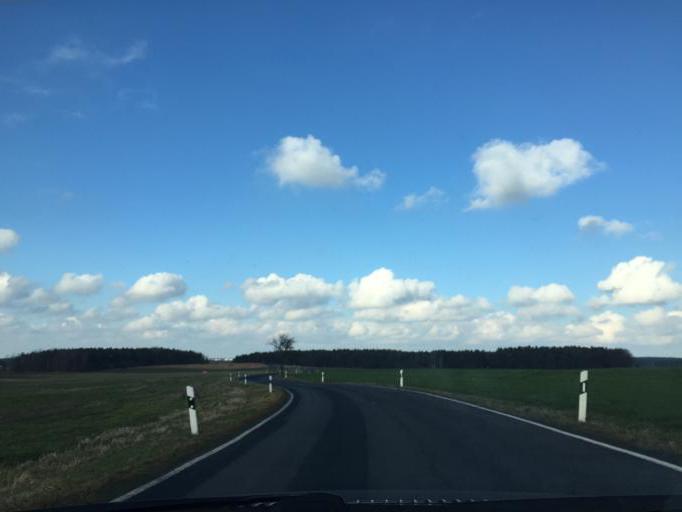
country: DE
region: Saxony
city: Tauscha
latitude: 51.2676
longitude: 13.7659
